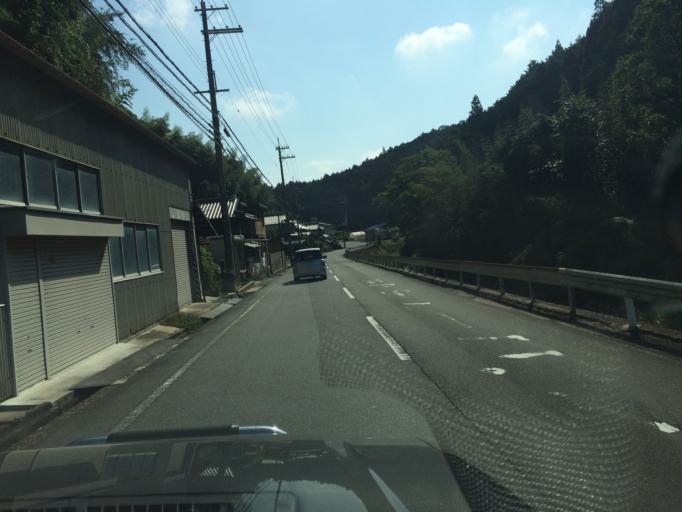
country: JP
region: Mie
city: Ueno-ebisumachi
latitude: 34.7355
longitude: 135.9716
